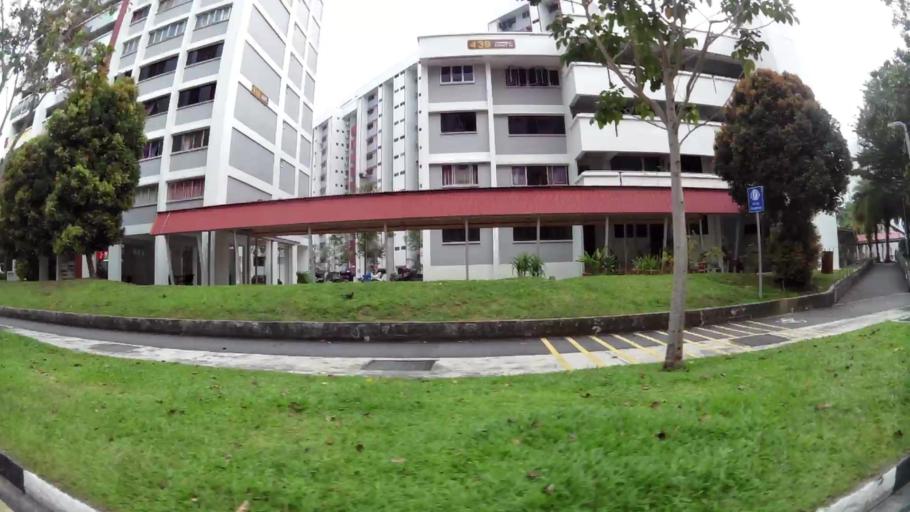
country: SG
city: Singapore
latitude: 1.3607
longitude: 103.9510
